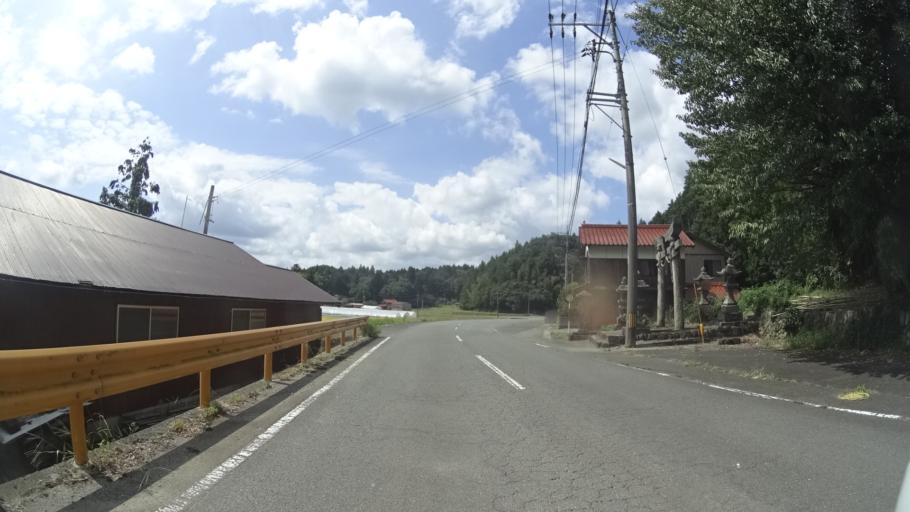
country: JP
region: Yamaguchi
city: Hagi
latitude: 34.5004
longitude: 131.5871
